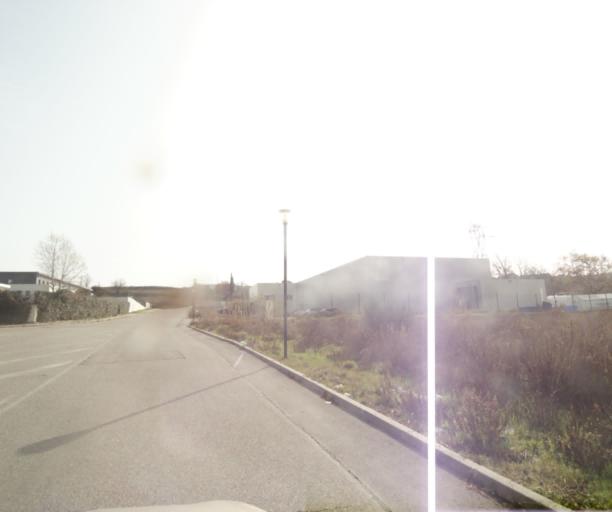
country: FR
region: Provence-Alpes-Cote d'Azur
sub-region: Departement des Bouches-du-Rhone
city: Gardanne
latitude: 43.4643
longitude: 5.4909
